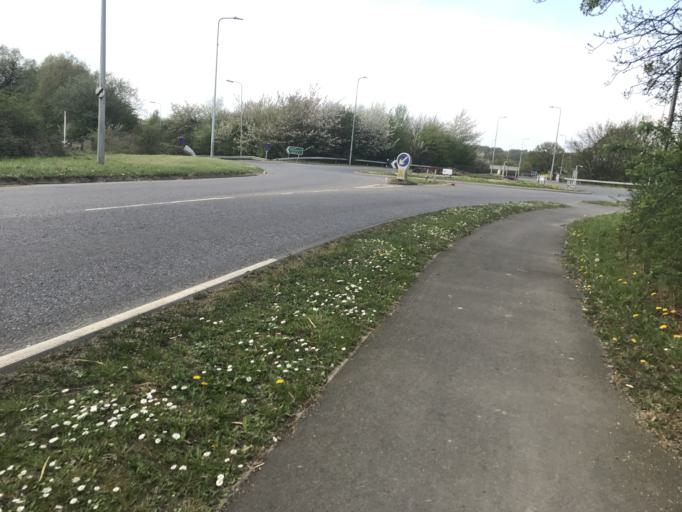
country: GB
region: England
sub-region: Essex
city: Stock
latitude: 51.6860
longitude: 0.4657
